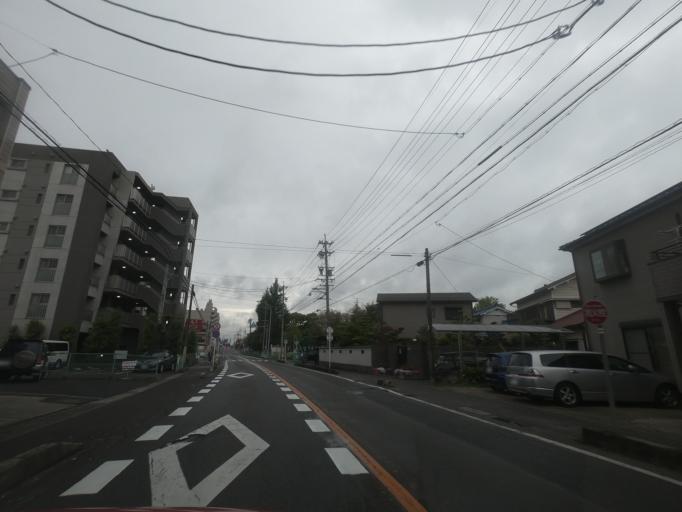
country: JP
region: Aichi
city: Kasugai
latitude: 35.2474
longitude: 136.9810
